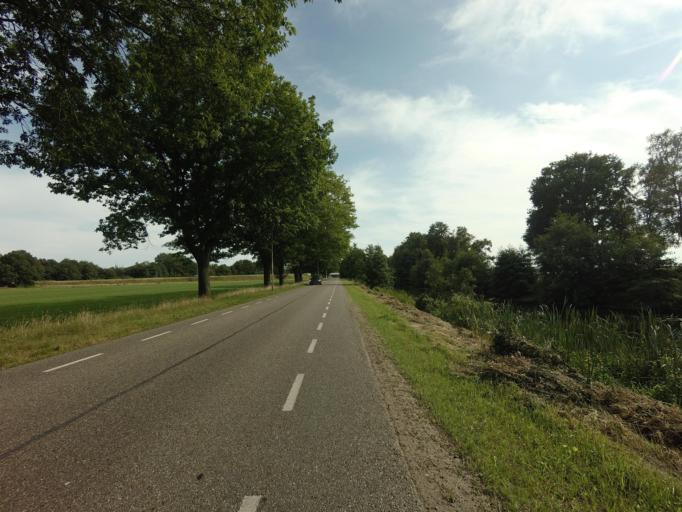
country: NL
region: Drenthe
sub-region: Gemeente Coevorden
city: Coevorden
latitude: 52.6726
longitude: 6.7229
